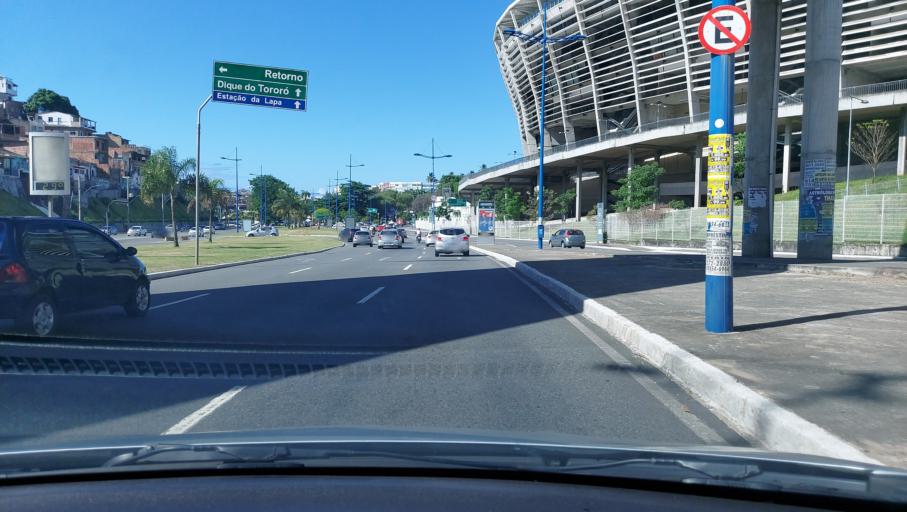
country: BR
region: Bahia
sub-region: Salvador
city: Salvador
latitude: -12.9789
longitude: -38.5026
